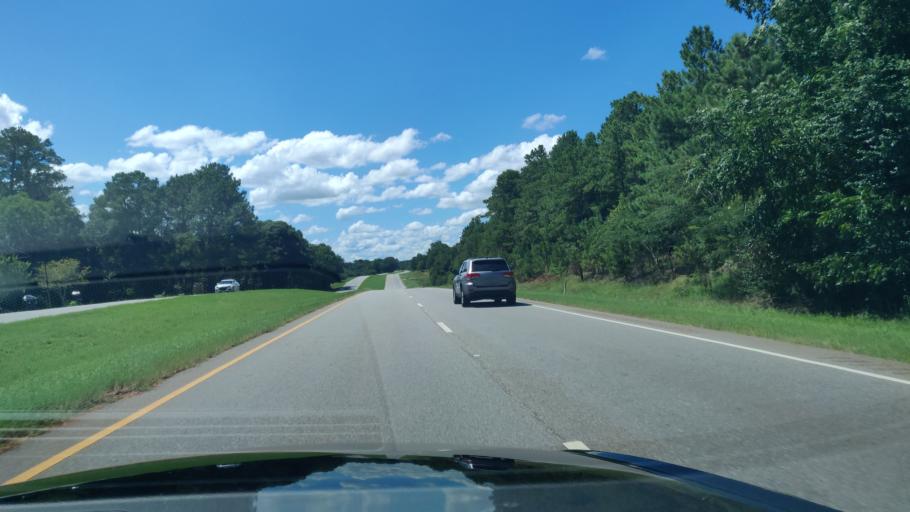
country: US
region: Georgia
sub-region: Terrell County
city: Dawson
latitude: 31.9036
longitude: -84.5234
